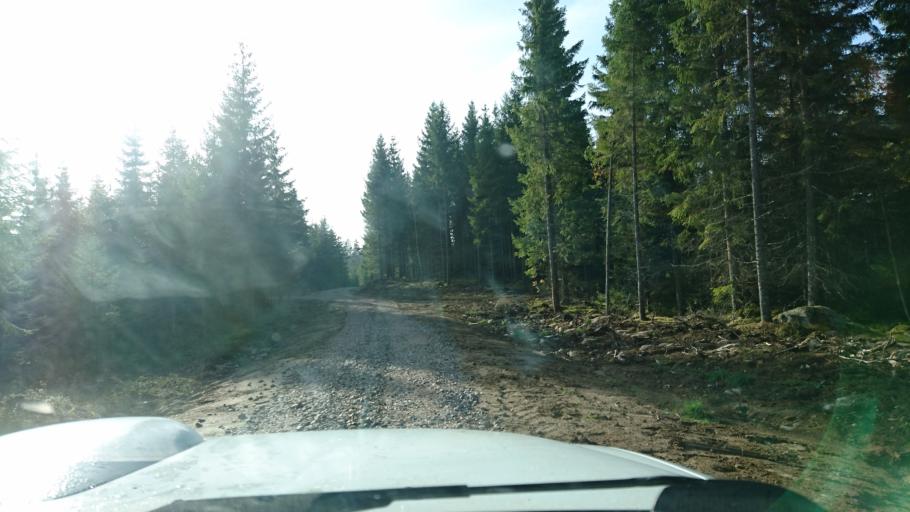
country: SE
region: Vaestra Goetaland
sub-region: Ulricehamns Kommun
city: Ulricehamn
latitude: 57.9410
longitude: 13.5516
